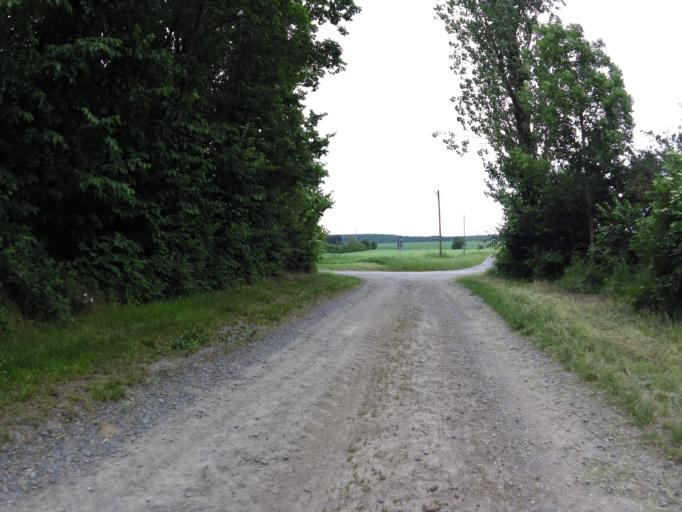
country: DE
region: Bavaria
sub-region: Regierungsbezirk Unterfranken
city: Waldbuttelbrunn
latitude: 49.8033
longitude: 9.8489
